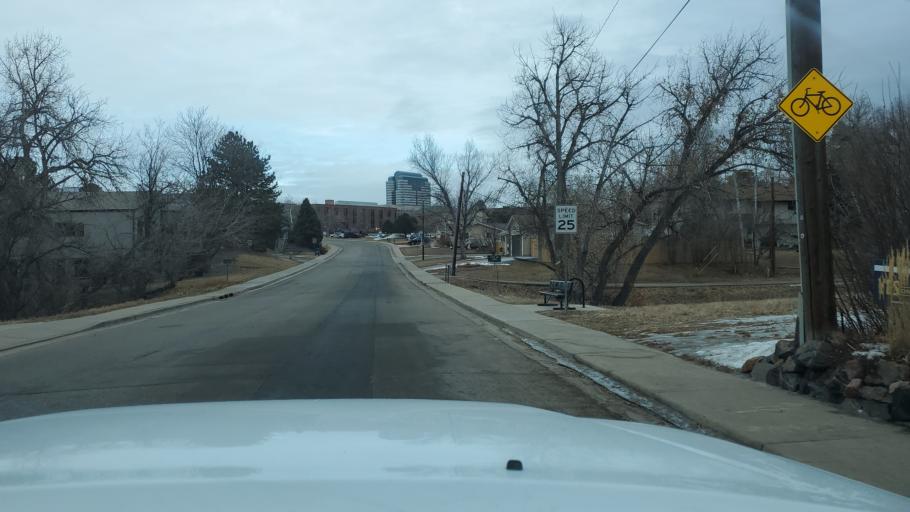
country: US
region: Colorado
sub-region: Arapahoe County
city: Castlewood
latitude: 39.5925
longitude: -104.8993
